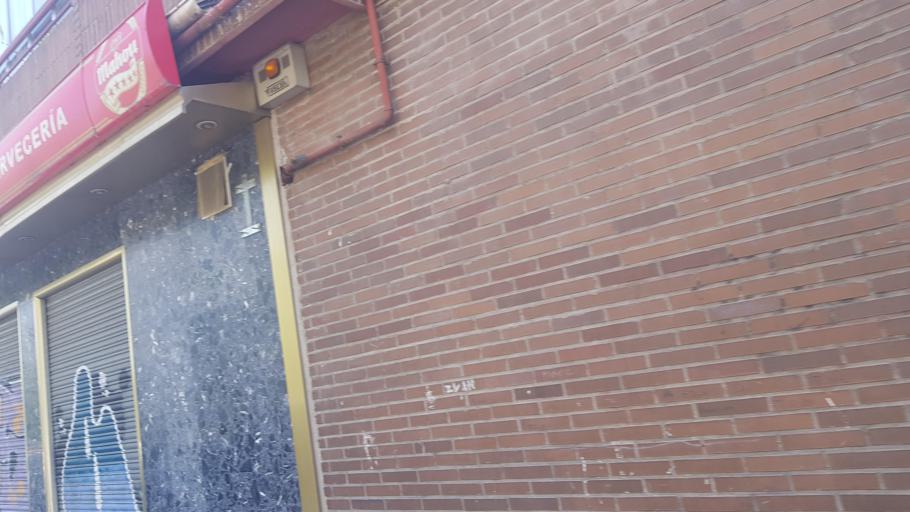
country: ES
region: Madrid
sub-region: Provincia de Madrid
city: Villaverde
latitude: 40.3491
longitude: -3.7123
